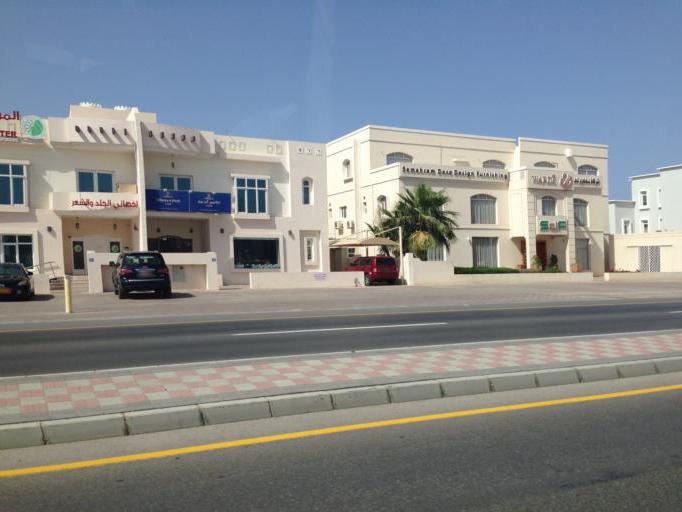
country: OM
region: Muhafazat Masqat
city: Bawshar
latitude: 23.6003
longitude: 58.3774
